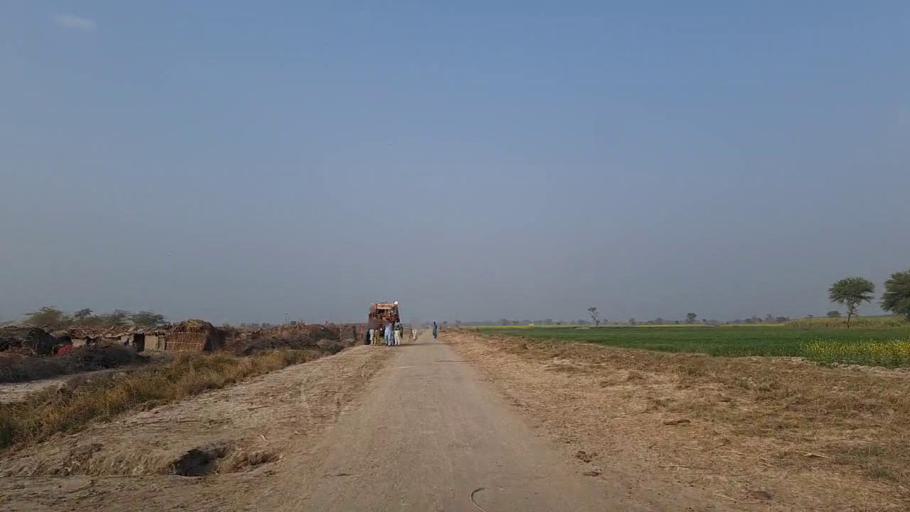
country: PK
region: Sindh
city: Jam Sahib
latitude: 26.3332
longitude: 68.5147
